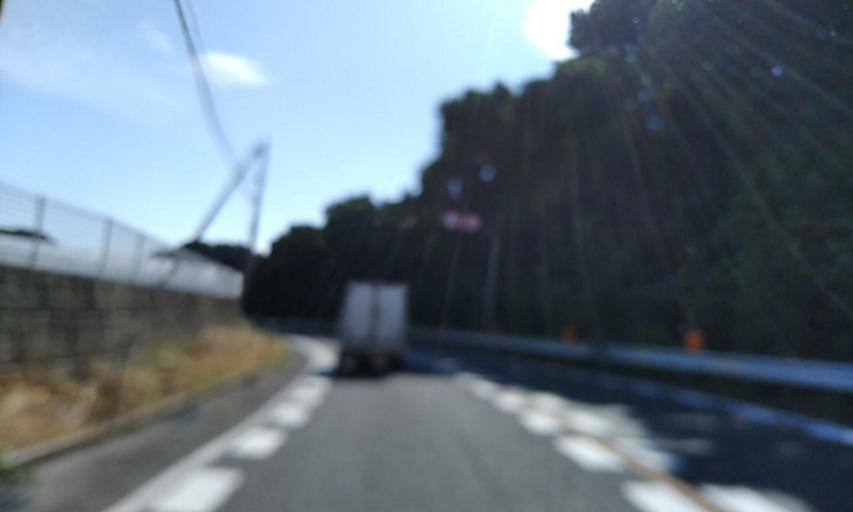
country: JP
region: Wakayama
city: Gobo
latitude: 33.7894
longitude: 135.2345
